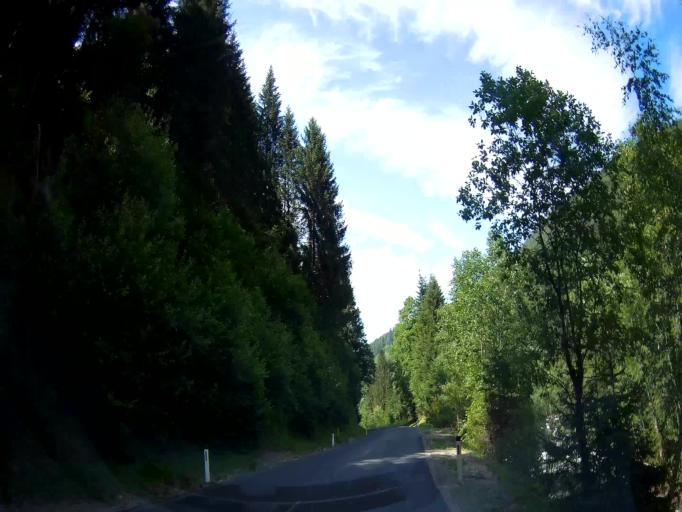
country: AT
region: Styria
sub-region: Politischer Bezirk Murau
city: Stadl an der Mur
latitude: 47.0506
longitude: 13.9972
